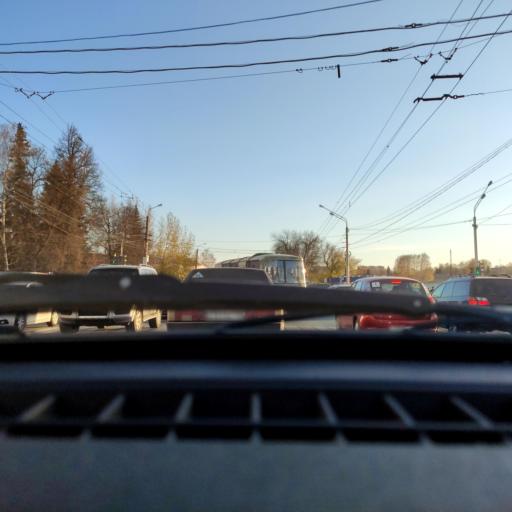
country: RU
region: Bashkortostan
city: Ufa
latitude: 54.7975
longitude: 56.1392
